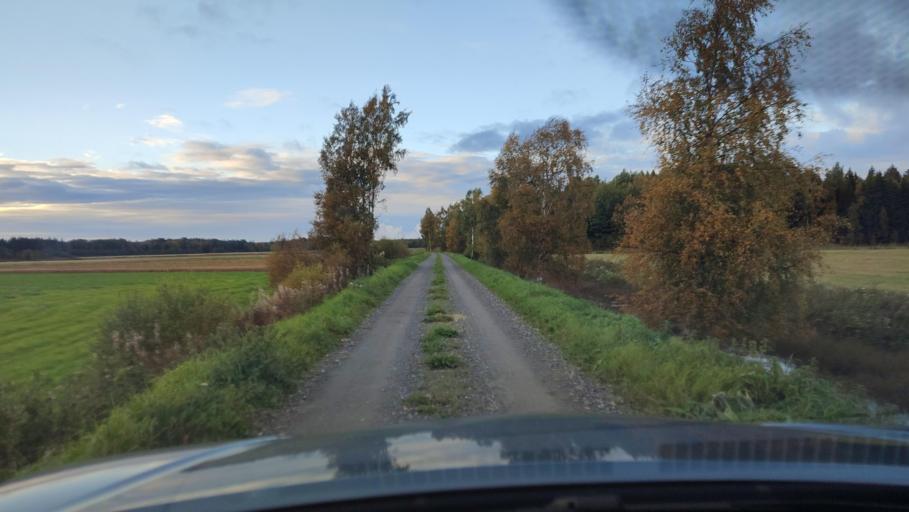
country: FI
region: Ostrobothnia
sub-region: Sydosterbotten
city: Kristinestad
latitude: 62.2433
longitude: 21.4532
